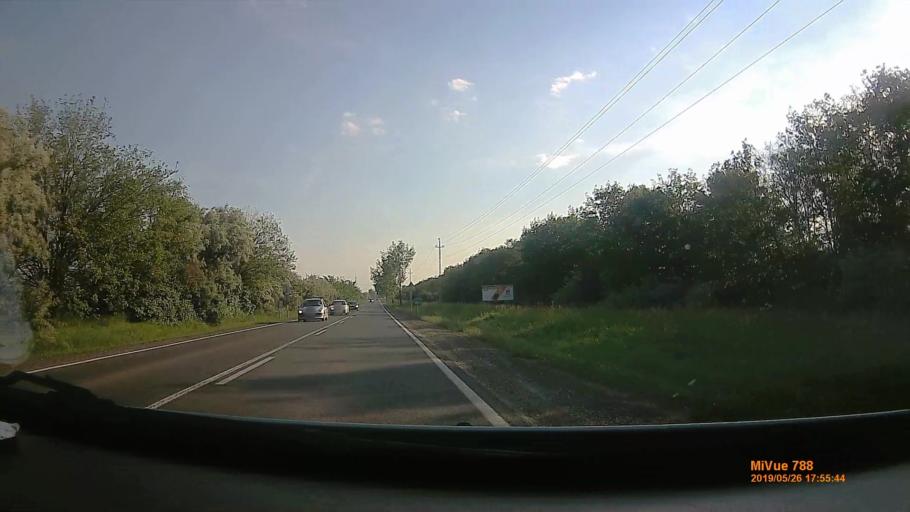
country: HU
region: Borsod-Abauj-Zemplen
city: Arnot
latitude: 48.1255
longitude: 20.8712
